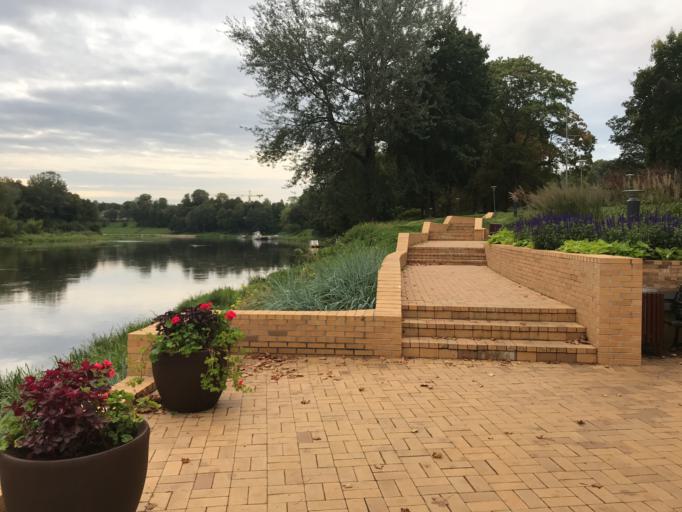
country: LT
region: Alytaus apskritis
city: Druskininkai
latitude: 54.0228
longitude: 23.9770
